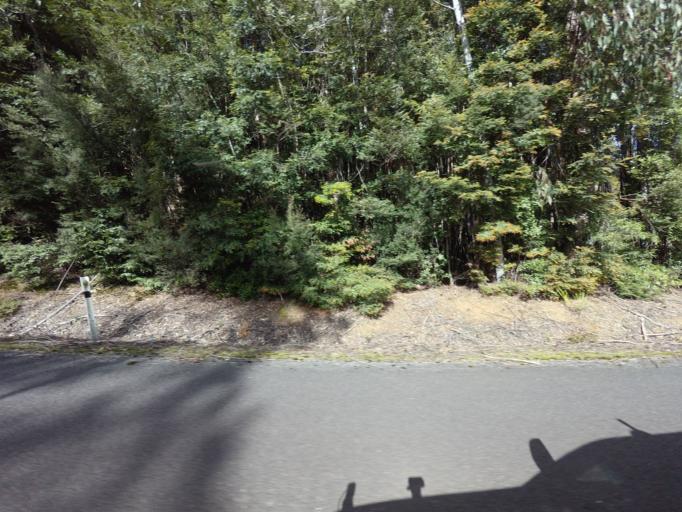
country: AU
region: Tasmania
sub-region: Huon Valley
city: Geeveston
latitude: -42.8238
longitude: 146.3142
